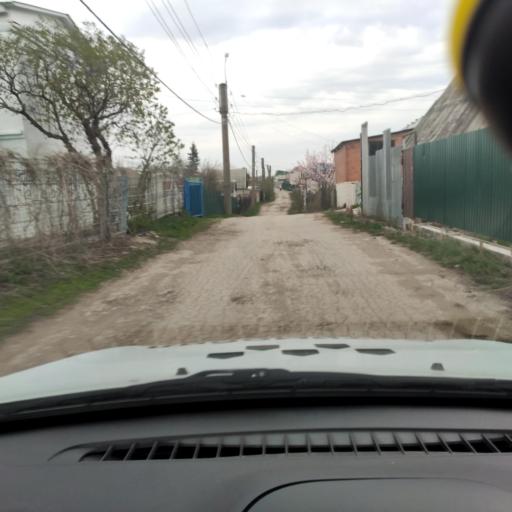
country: RU
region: Samara
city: Mezhdurechensk
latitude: 53.2449
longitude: 49.1490
